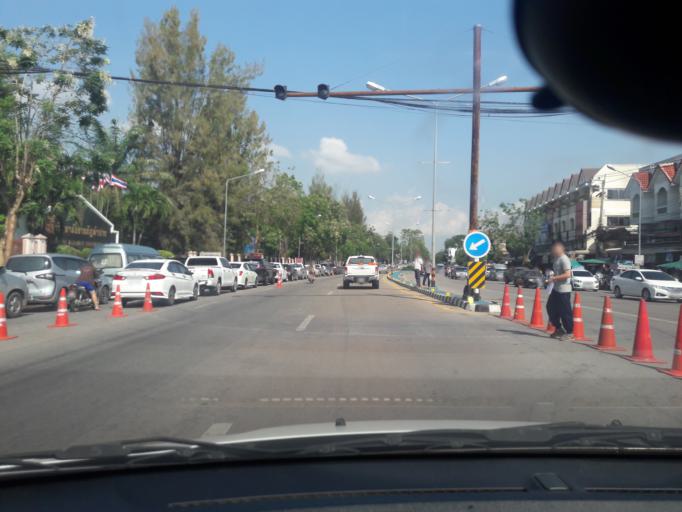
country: TH
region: Lampang
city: Lampang
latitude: 18.2364
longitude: 99.4905
